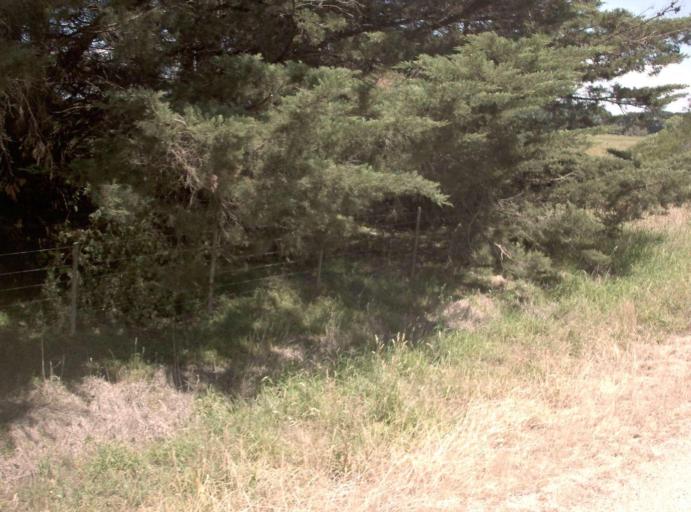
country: AU
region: Victoria
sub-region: Wellington
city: Heyfield
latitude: -38.0310
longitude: 146.8792
